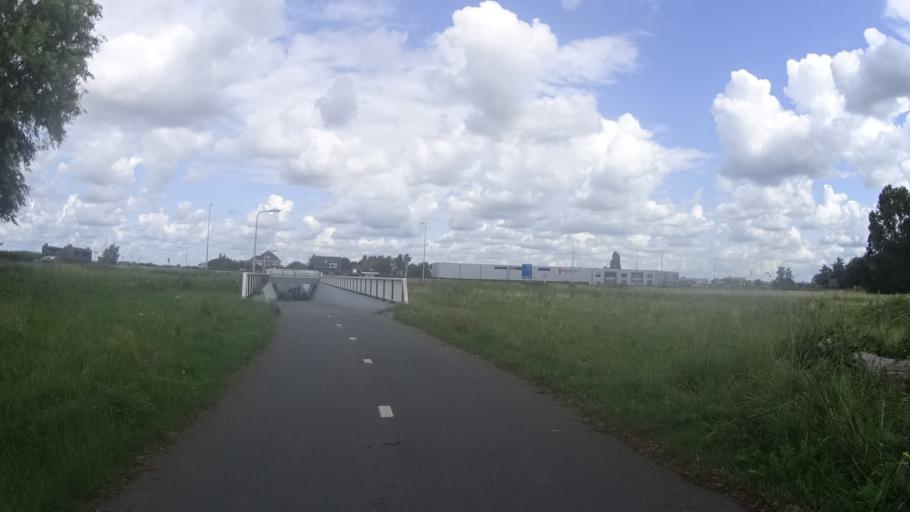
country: NL
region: North Holland
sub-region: Gemeente Beverwijk
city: Beverwijk
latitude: 52.4986
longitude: 4.6501
